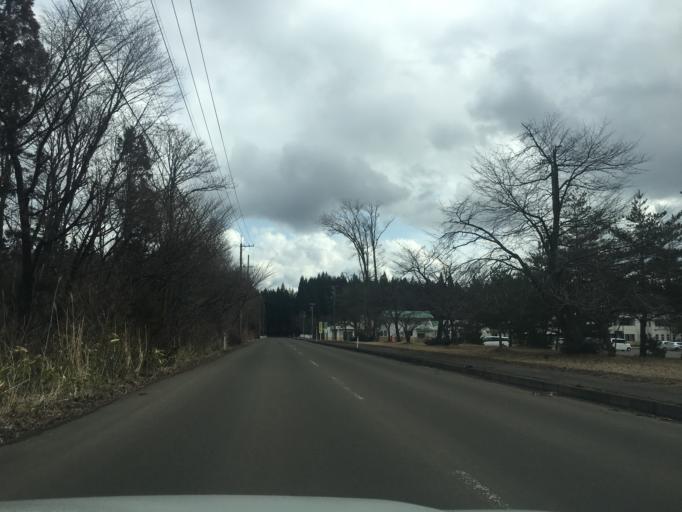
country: JP
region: Akita
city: Takanosu
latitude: 40.1872
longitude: 140.3504
